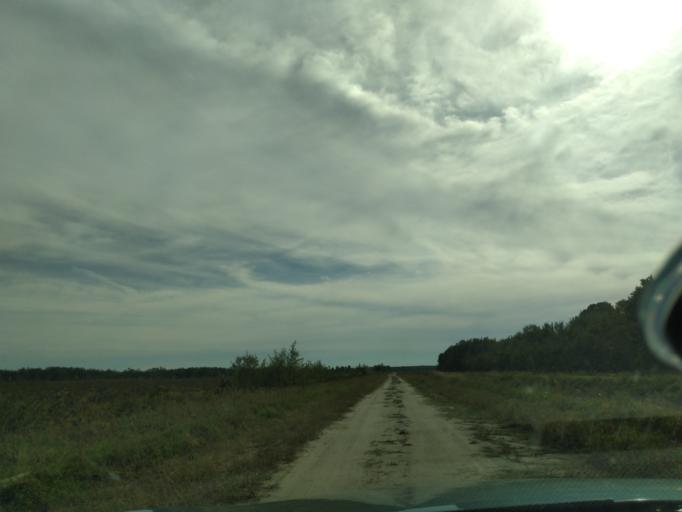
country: US
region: North Carolina
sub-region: Beaufort County
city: Belhaven
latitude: 35.7163
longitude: -76.5771
